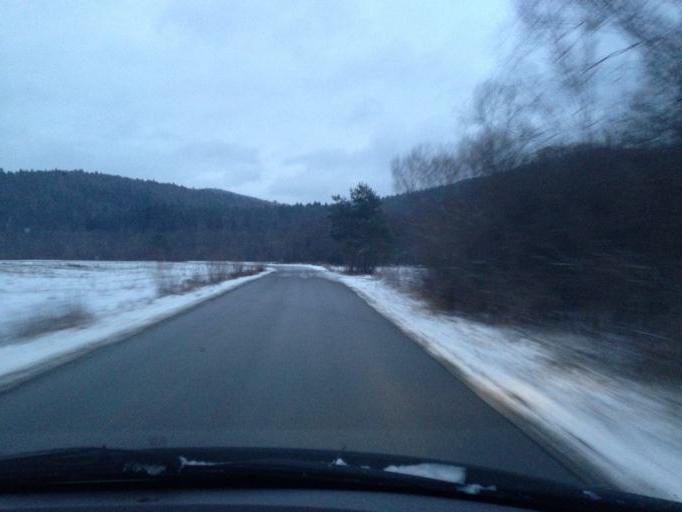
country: PL
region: Subcarpathian Voivodeship
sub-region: Powiat jasielski
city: Krempna
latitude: 49.5047
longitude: 21.5220
